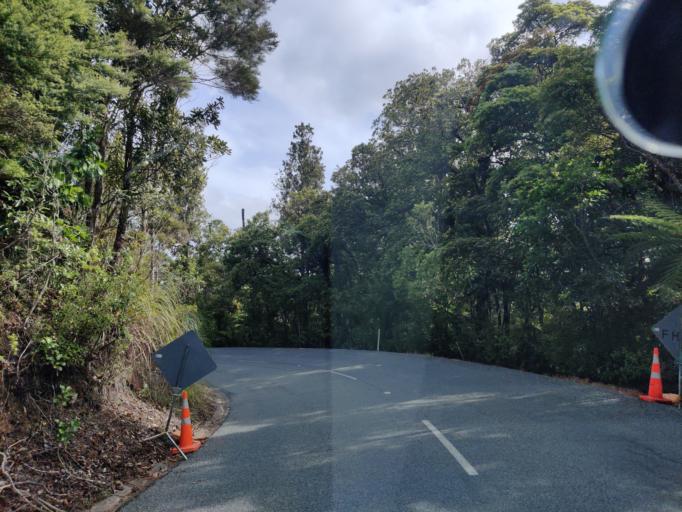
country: NZ
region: Northland
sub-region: Kaipara District
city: Dargaville
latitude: -35.6471
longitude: 173.5600
